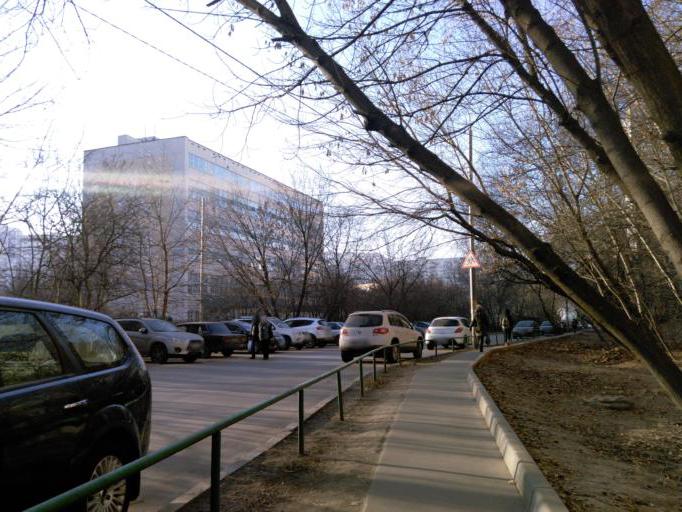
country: RU
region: Moscow
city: Troparevo
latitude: 55.6541
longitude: 37.4888
